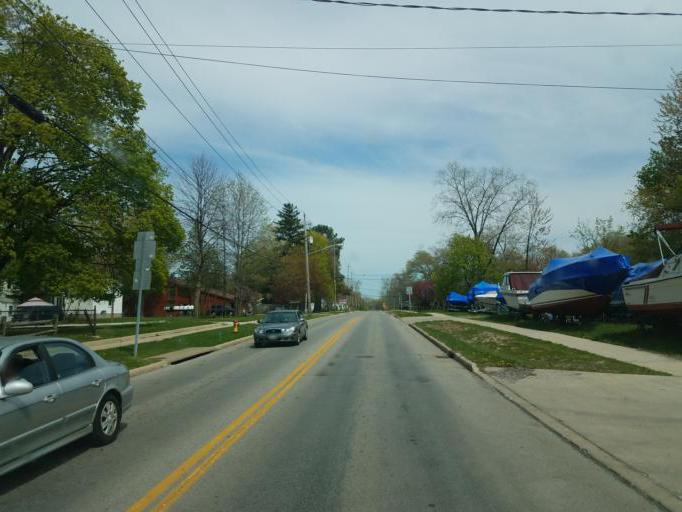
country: US
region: Ohio
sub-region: Lake County
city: Mentor-on-the-Lake
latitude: 41.7197
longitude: -81.3611
